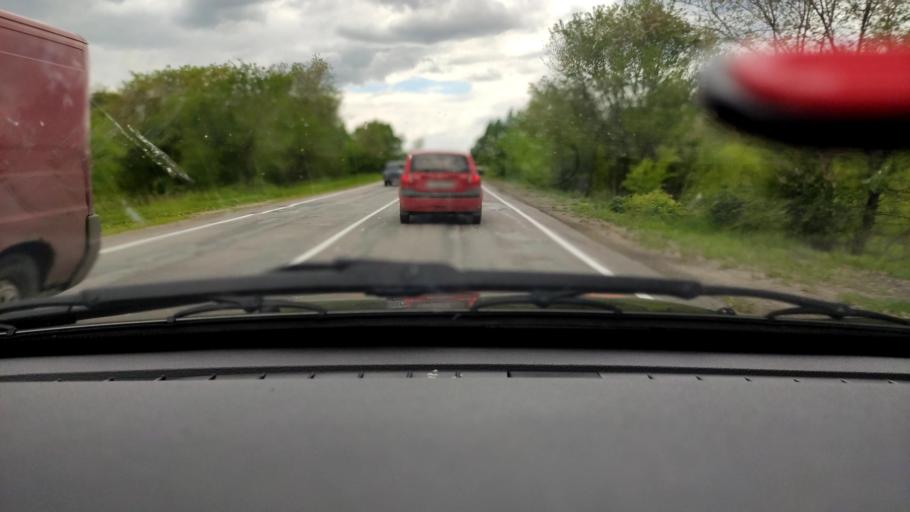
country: RU
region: Belgorod
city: Krasnoye
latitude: 51.0679
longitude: 38.8064
